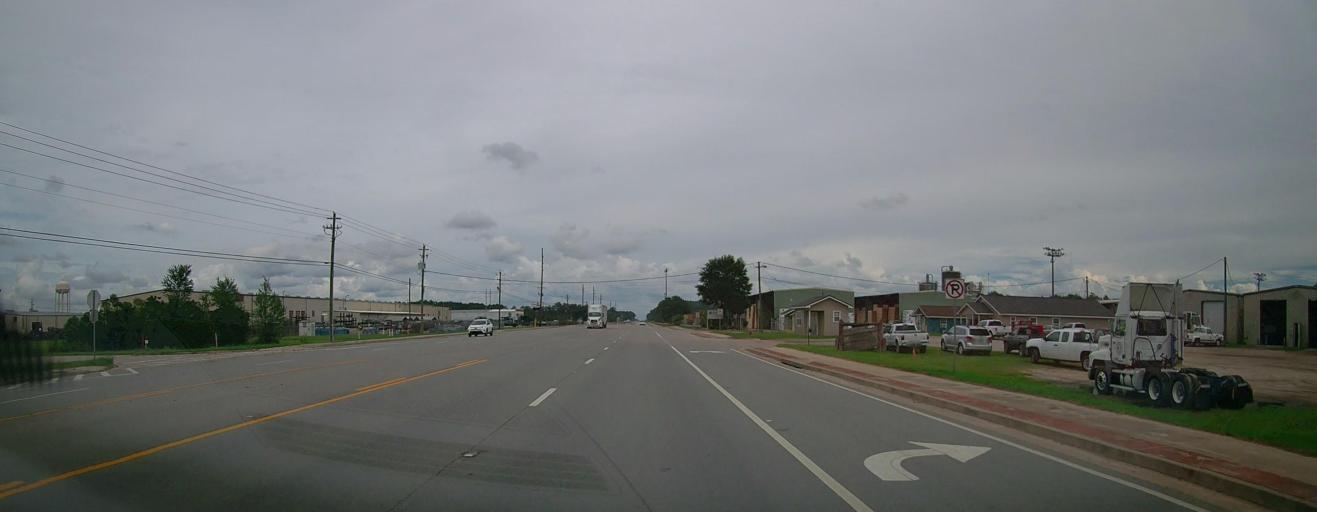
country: US
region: Georgia
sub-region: Appling County
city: Baxley
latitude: 31.7709
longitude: -82.3263
